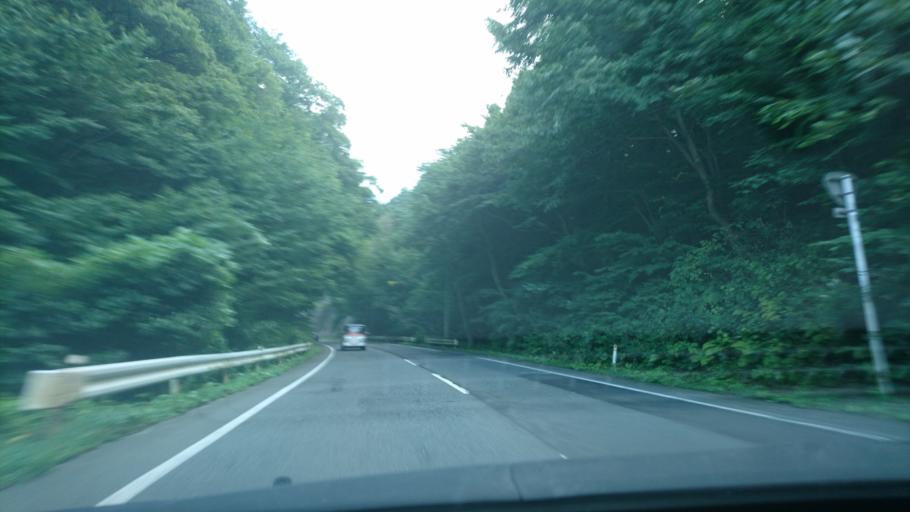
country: JP
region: Iwate
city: Mizusawa
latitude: 39.0615
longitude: 141.2240
